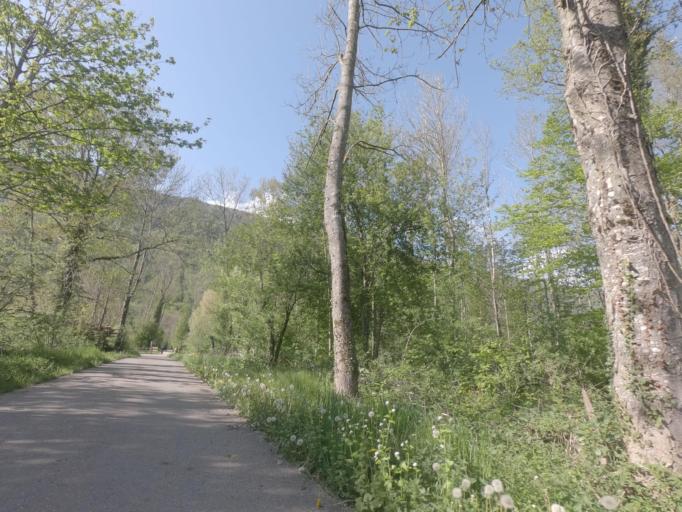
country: CH
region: Bern
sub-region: Biel/Bienne District
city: Orpund
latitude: 47.1651
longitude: 7.3026
